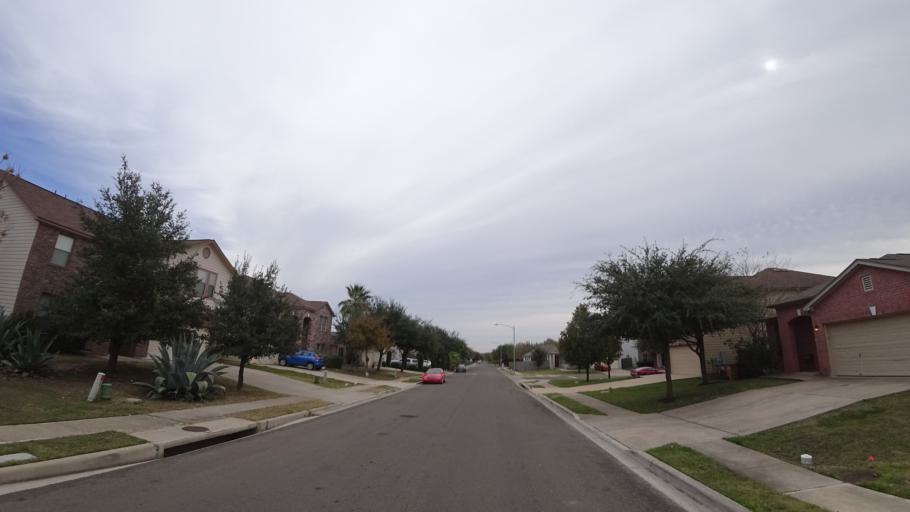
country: US
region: Texas
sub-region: Travis County
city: Onion Creek
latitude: 30.1606
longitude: -97.7422
